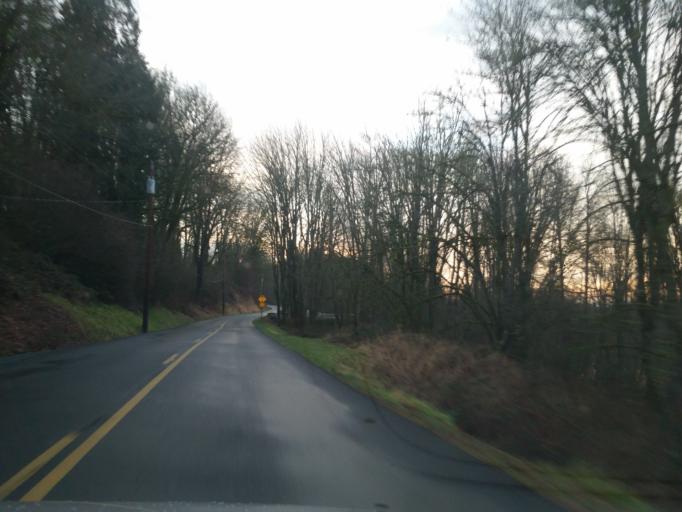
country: US
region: Washington
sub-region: Snohomish County
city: Cathcart
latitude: 47.8586
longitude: -122.0936
